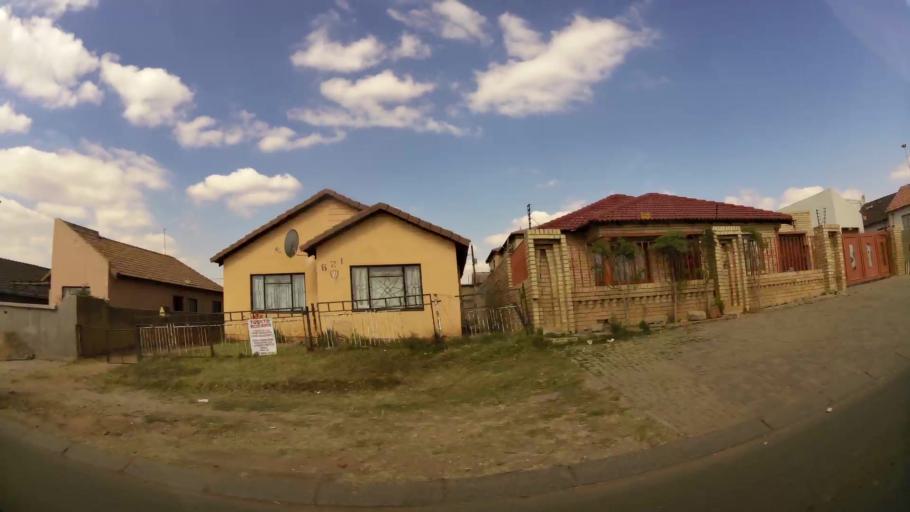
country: ZA
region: Gauteng
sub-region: Ekurhuleni Metropolitan Municipality
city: Tembisa
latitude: -25.9959
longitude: 28.2157
